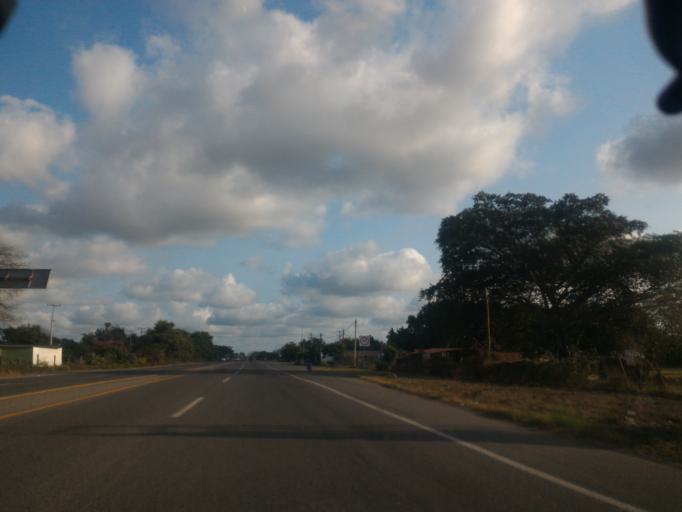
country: MX
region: Colima
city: Tecoman
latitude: 18.8962
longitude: -103.8584
